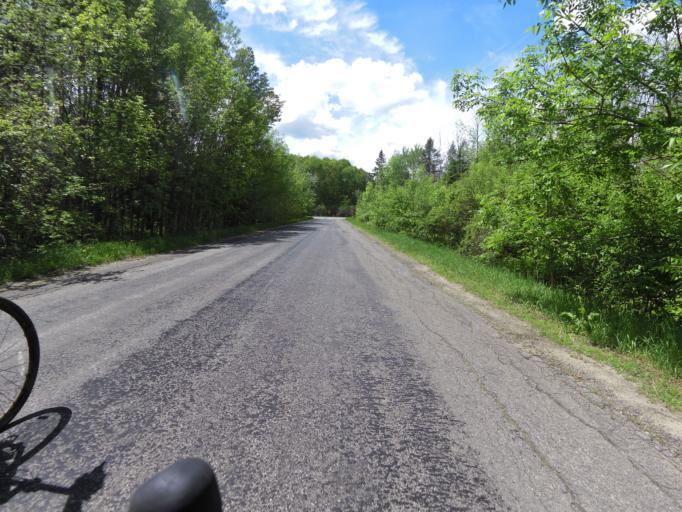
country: CA
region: Ontario
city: Ottawa
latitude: 45.4087
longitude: -75.5594
